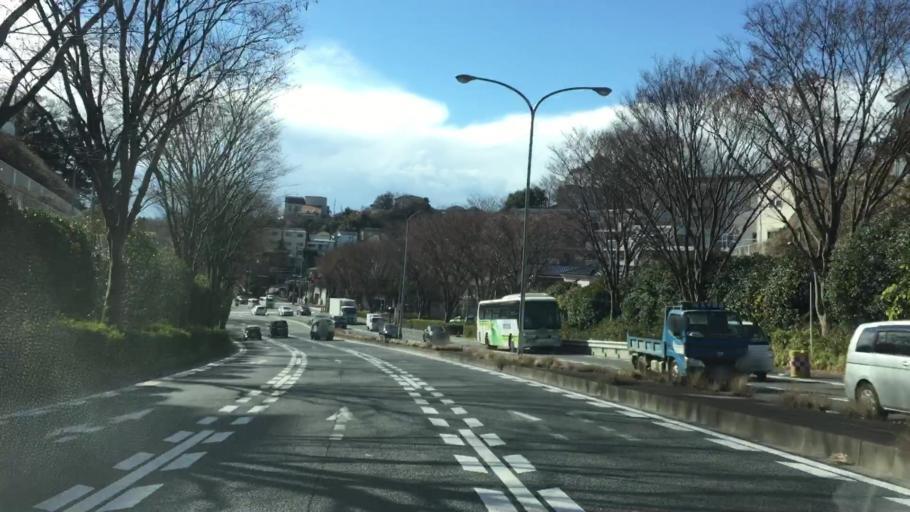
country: JP
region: Kanagawa
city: Yokohama
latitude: 35.4785
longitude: 139.5780
